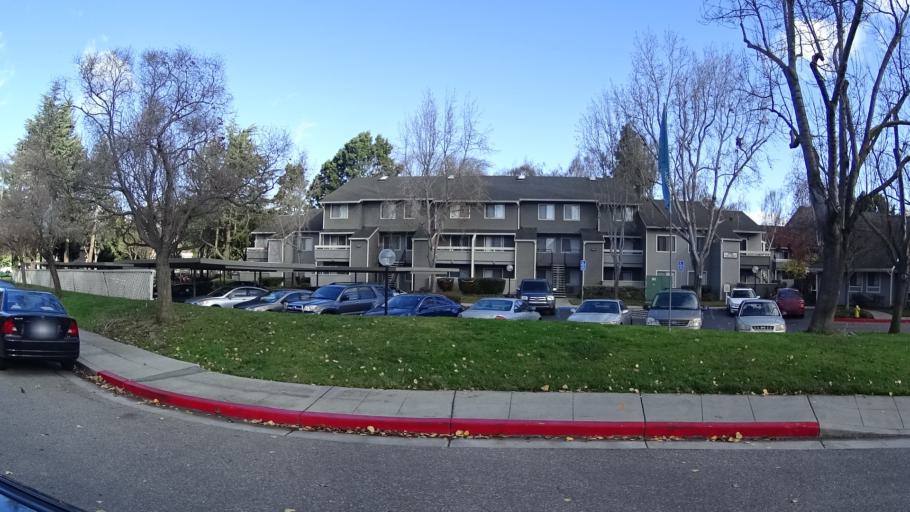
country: US
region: California
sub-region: Santa Clara County
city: Sunnyvale
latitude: 37.3830
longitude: -122.0408
